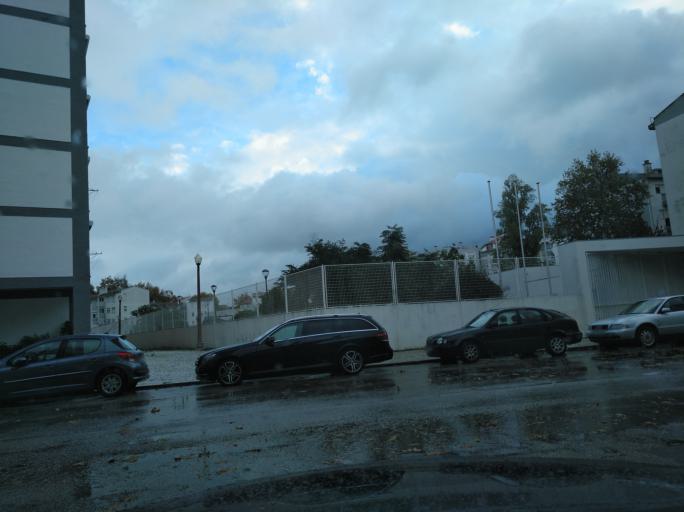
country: PT
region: Lisbon
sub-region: Loures
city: Moscavide
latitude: 38.7595
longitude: -9.1102
